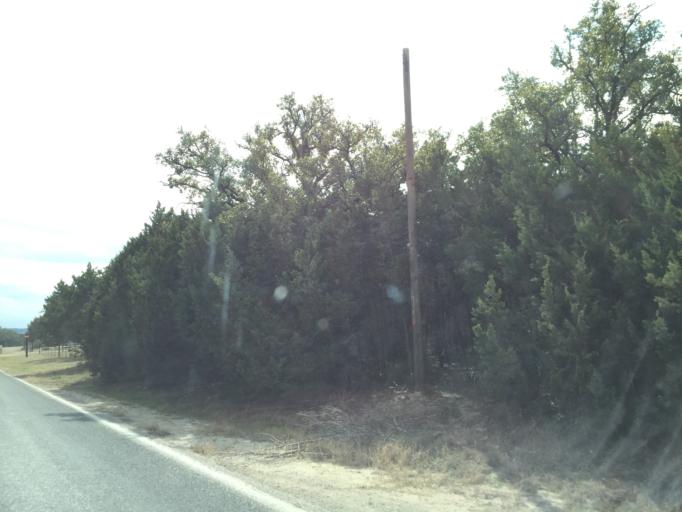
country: US
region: Texas
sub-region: Travis County
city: Briarcliff
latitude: 30.3818
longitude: -98.0955
